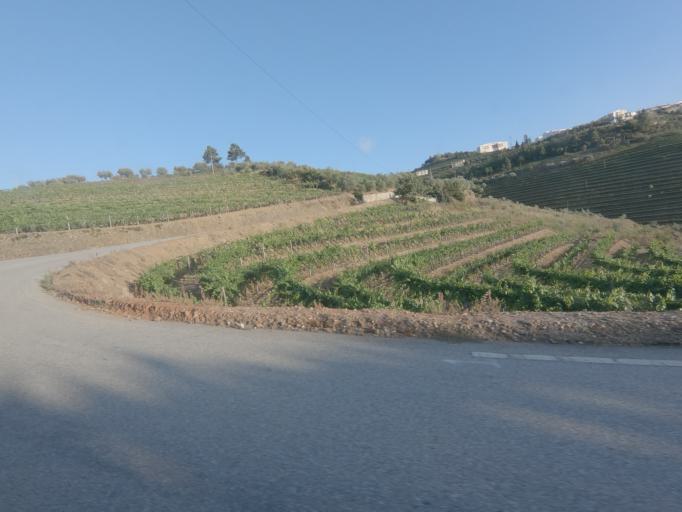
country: PT
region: Viseu
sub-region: Armamar
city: Armamar
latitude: 41.1137
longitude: -7.6865
